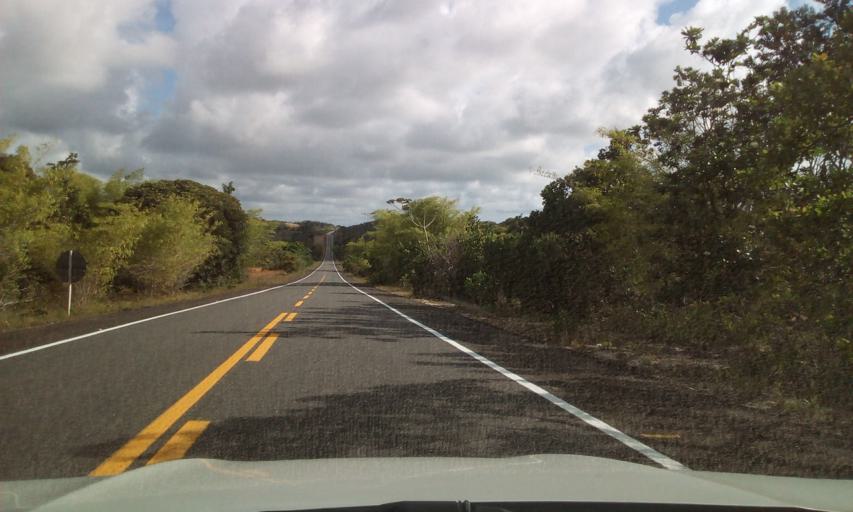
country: BR
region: Bahia
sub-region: Conde
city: Conde
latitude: -11.6812
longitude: -37.5652
